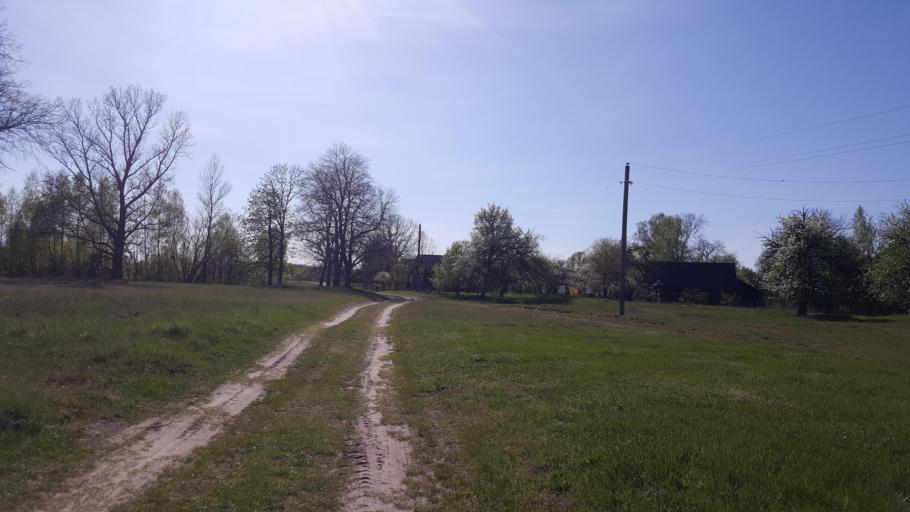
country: BY
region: Brest
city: Kamyanyets
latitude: 52.4393
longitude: 23.9001
